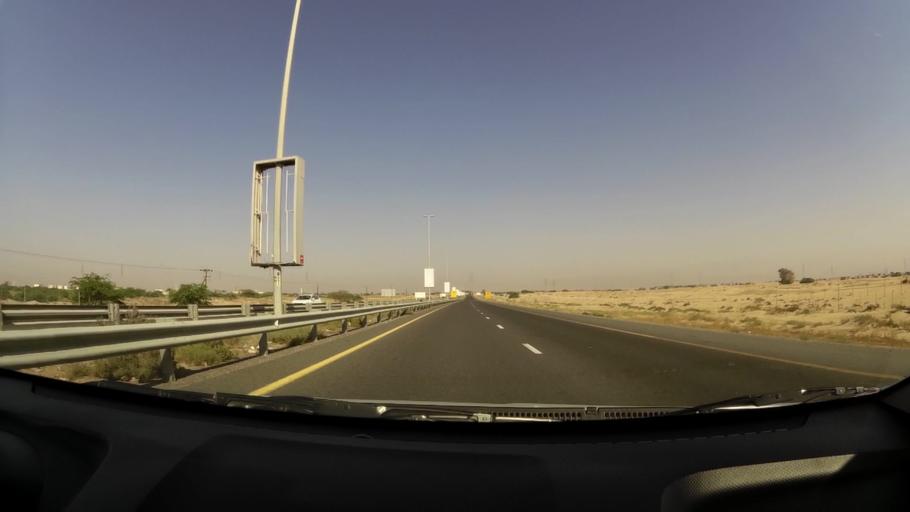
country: AE
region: Umm al Qaywayn
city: Umm al Qaywayn
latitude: 25.4756
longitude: 55.5726
